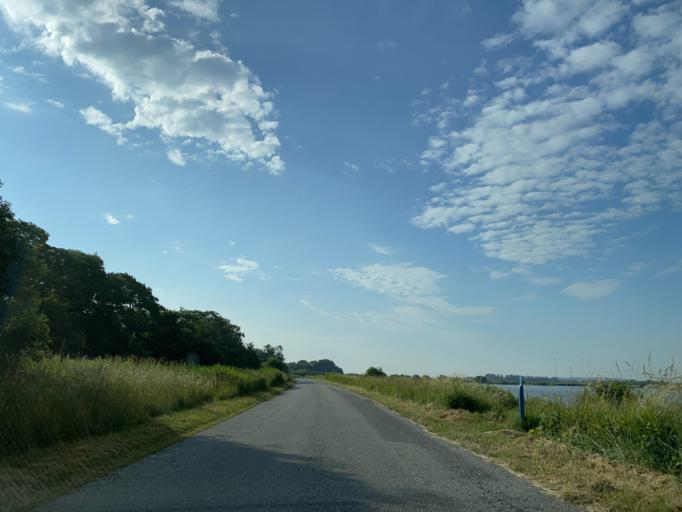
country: DK
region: South Denmark
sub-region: Haderslev Kommune
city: Haderslev
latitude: 55.1714
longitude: 9.4862
